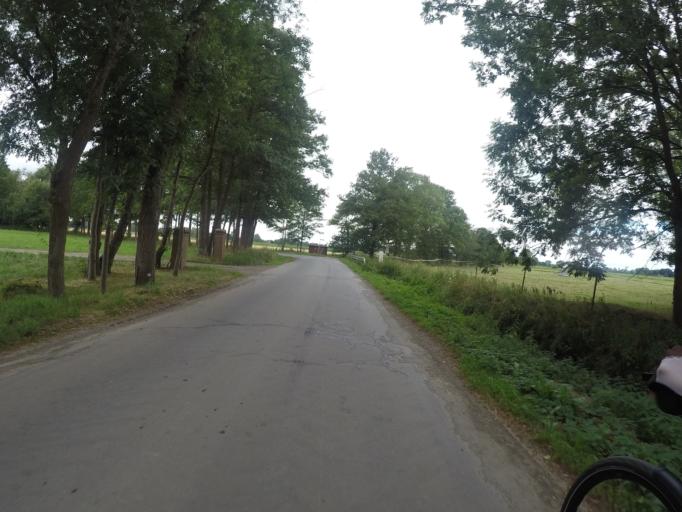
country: DE
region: Lower Saxony
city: Grossenworden
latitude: 53.6851
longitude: 9.2376
